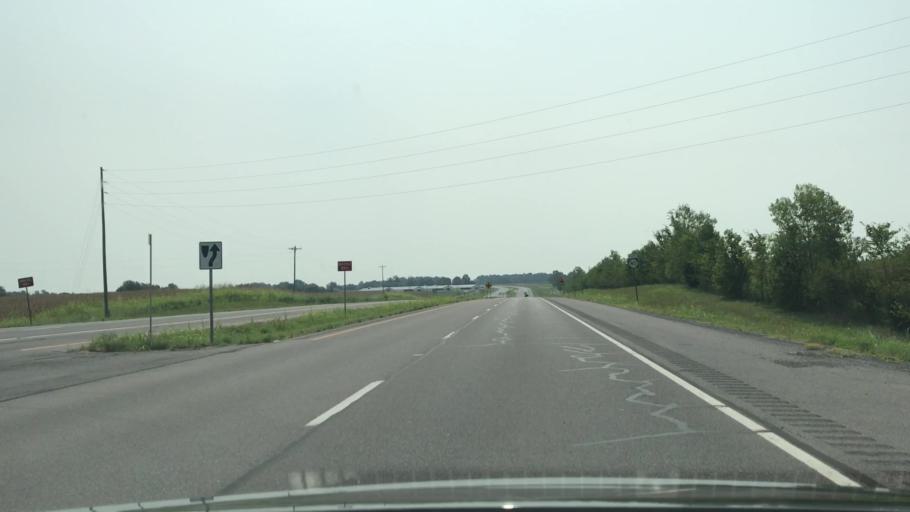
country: US
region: Kentucky
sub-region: Graves County
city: Mayfield
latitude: 36.6838
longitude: -88.5379
